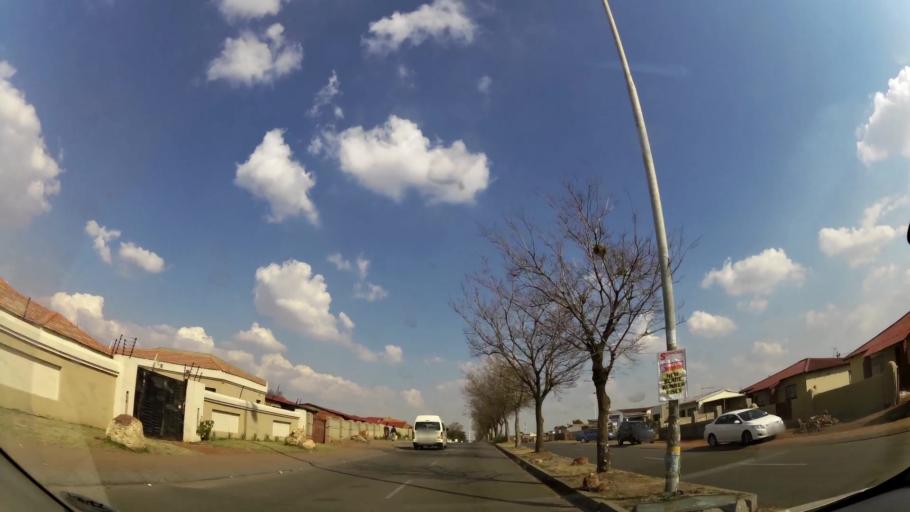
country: ZA
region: Gauteng
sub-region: Ekurhuleni Metropolitan Municipality
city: Germiston
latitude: -26.3186
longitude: 28.1578
